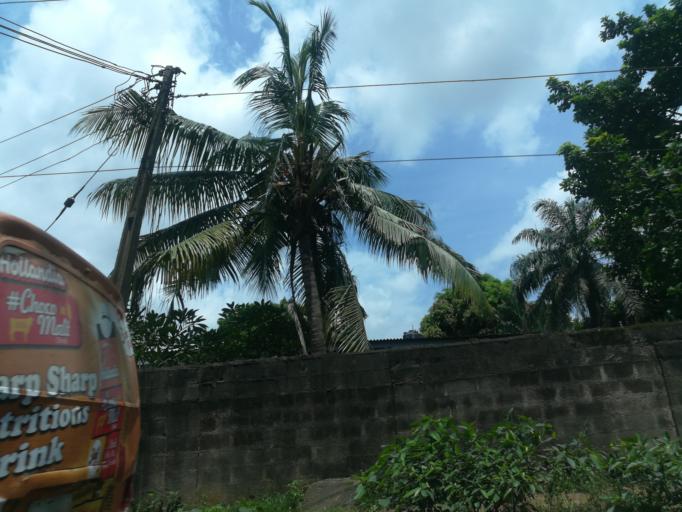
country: NG
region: Lagos
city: Somolu
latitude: 6.5445
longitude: 3.3624
